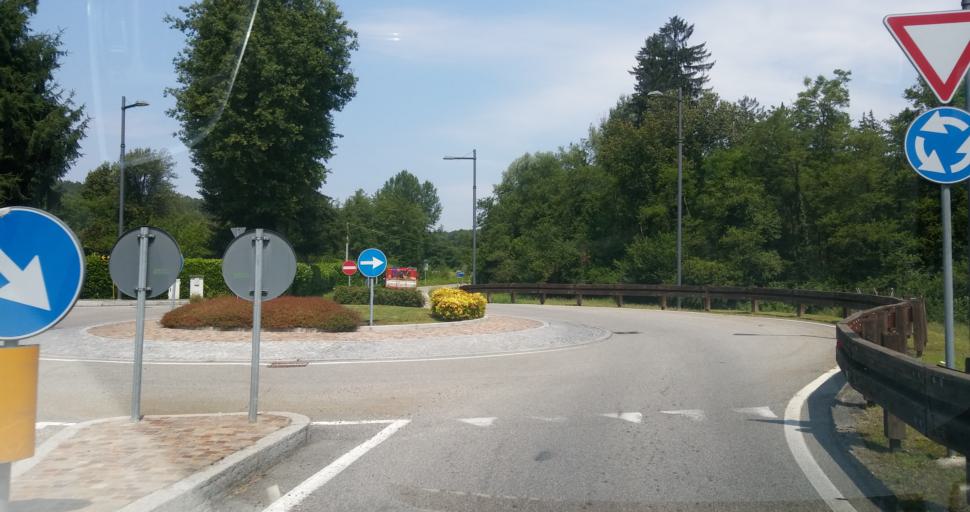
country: IT
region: Lombardy
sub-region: Provincia di Varese
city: Sesto Calende
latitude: 45.7430
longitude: 8.6415
